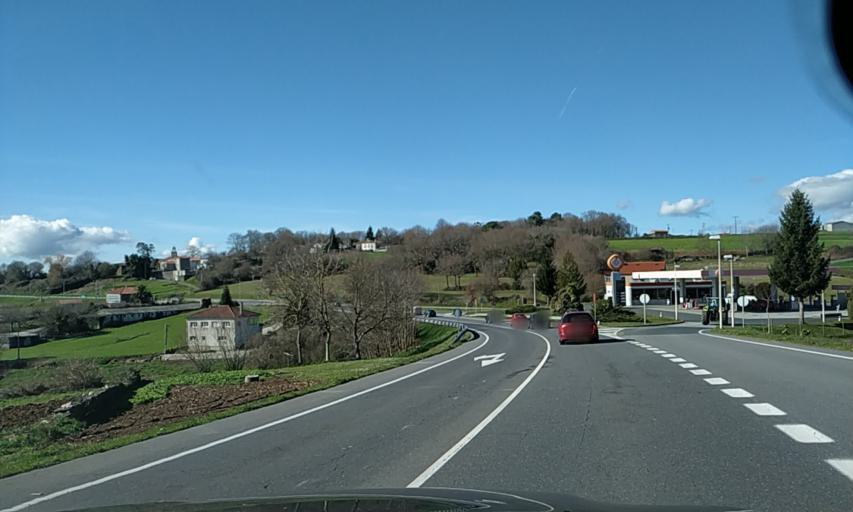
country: ES
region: Galicia
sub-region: Provincia de Pontevedra
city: Lalin
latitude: 42.6819
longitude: -8.1674
